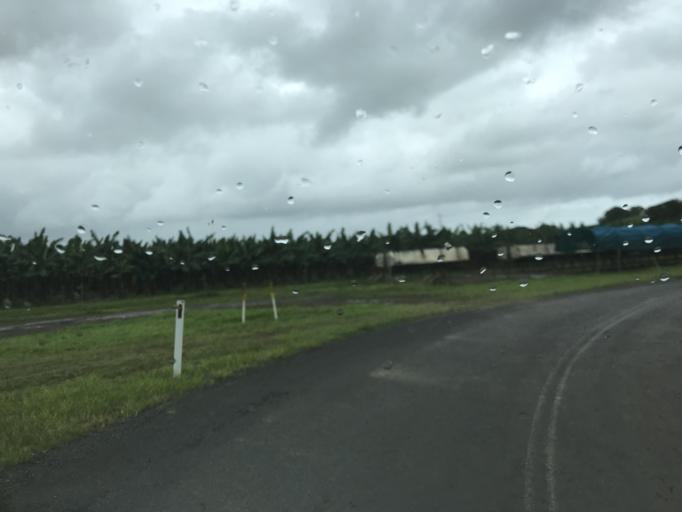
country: AU
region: Queensland
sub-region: Cassowary Coast
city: Innisfail
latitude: -17.5154
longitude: 145.9786
